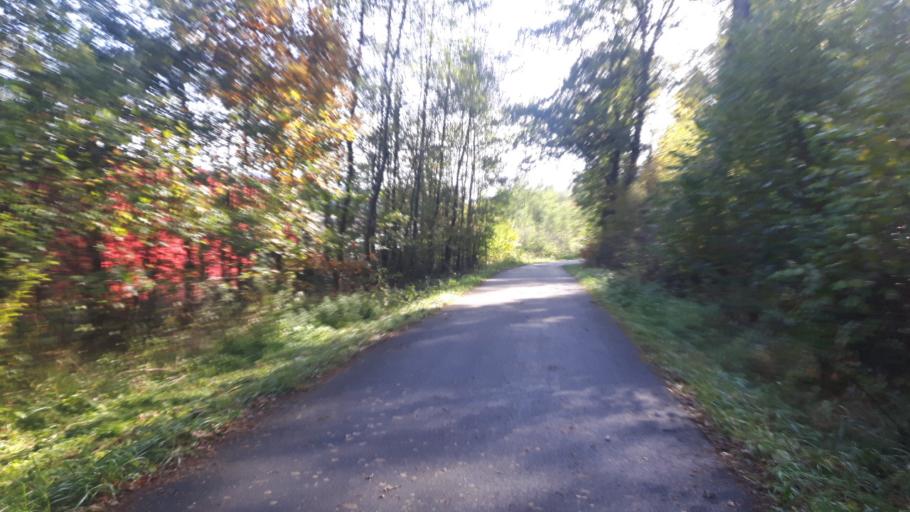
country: DE
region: North Rhine-Westphalia
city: Netphen
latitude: 50.8873
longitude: 8.1242
